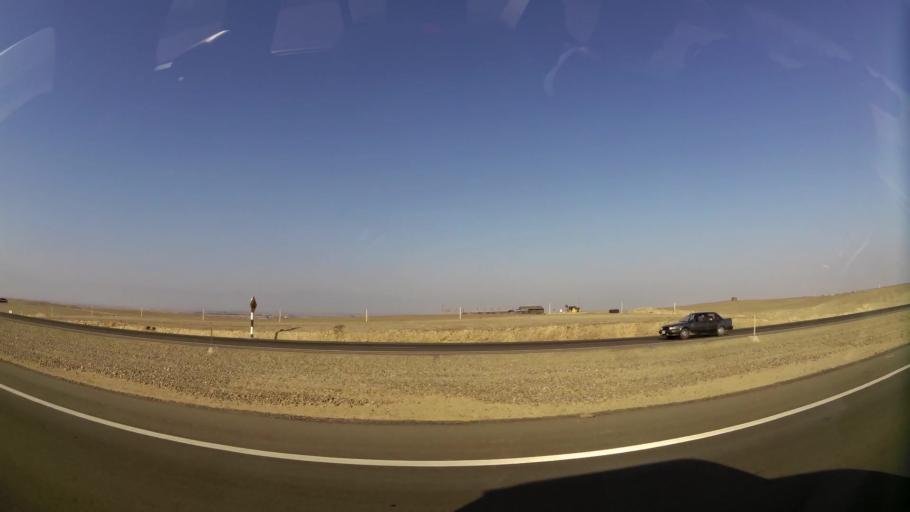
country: PE
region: Ica
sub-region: Provincia de Pisco
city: San Clemente
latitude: -13.6474
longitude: -76.1736
